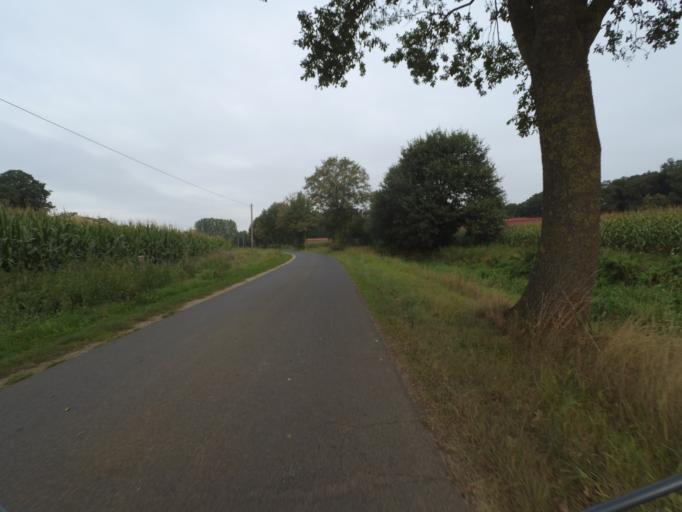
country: DE
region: Lower Saxony
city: Isterberg
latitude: 52.3304
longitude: 7.0653
